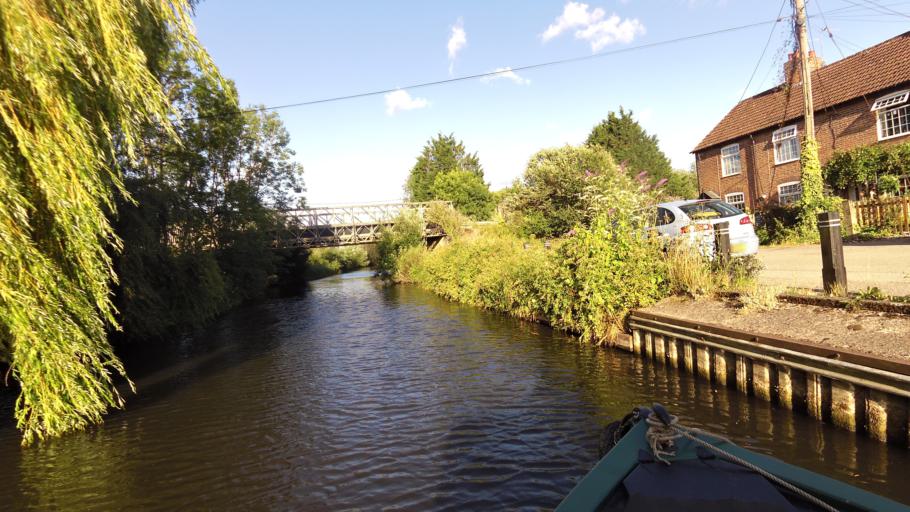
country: GB
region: England
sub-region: West Berkshire
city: Thatcham
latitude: 51.3936
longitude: -1.2256
